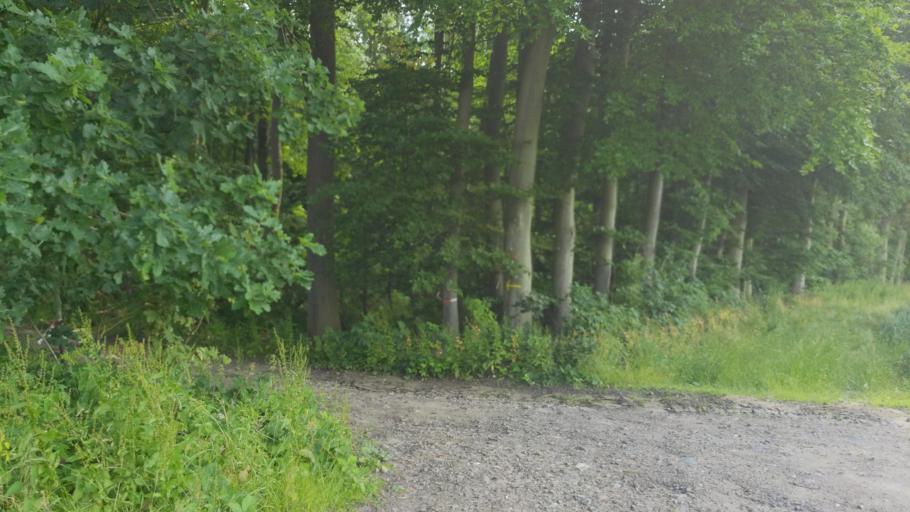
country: DE
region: Schleswig-Holstein
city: Gromitz
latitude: 54.1301
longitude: 10.9366
